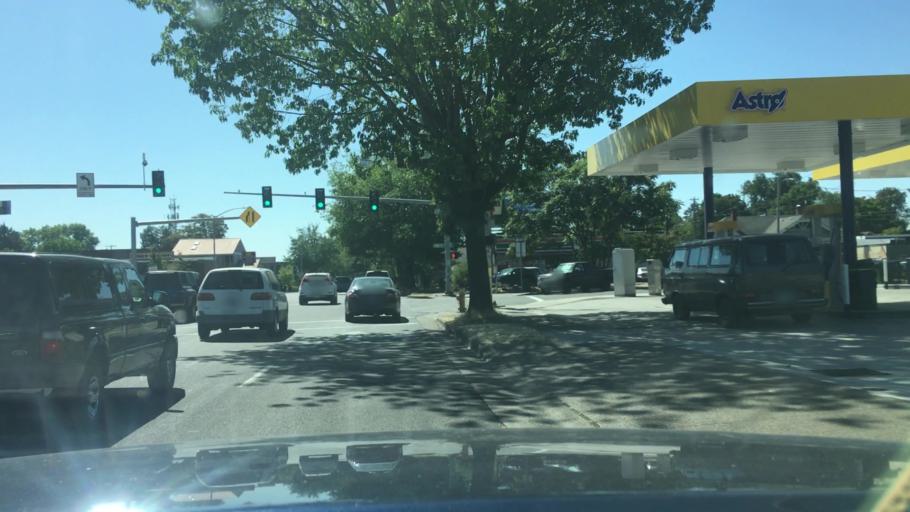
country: US
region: Oregon
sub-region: Lane County
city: Eugene
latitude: 44.0533
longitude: -123.1066
